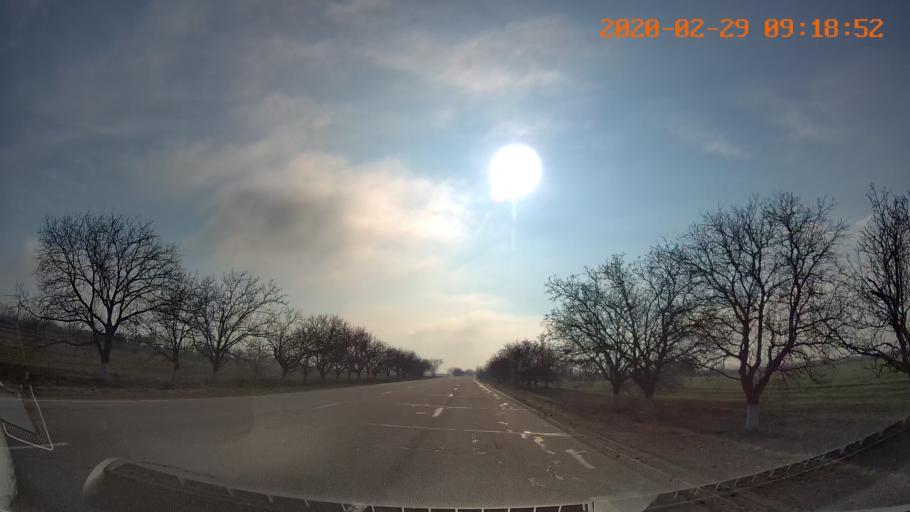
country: MD
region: Telenesti
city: Pervomaisc
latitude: 46.7695
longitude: 29.9310
